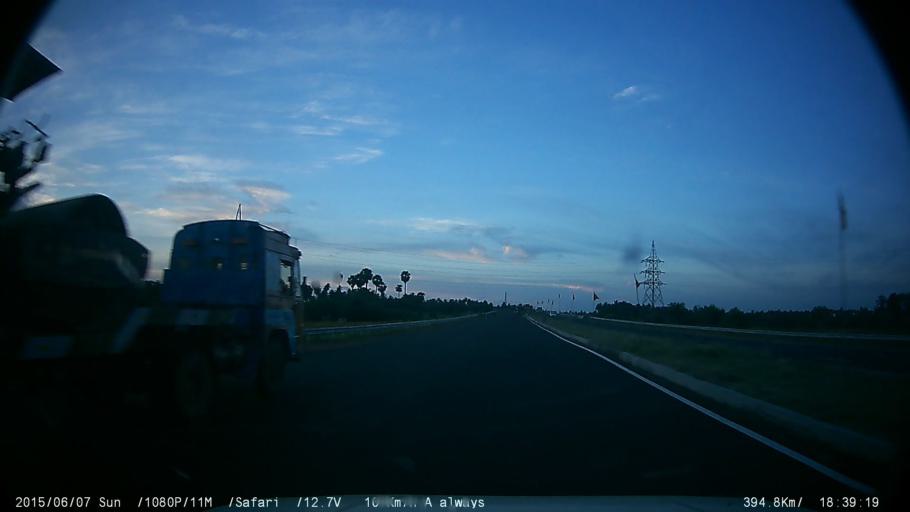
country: IN
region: Tamil Nadu
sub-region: Tiruppur
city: Avinashi
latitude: 11.2089
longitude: 77.3427
